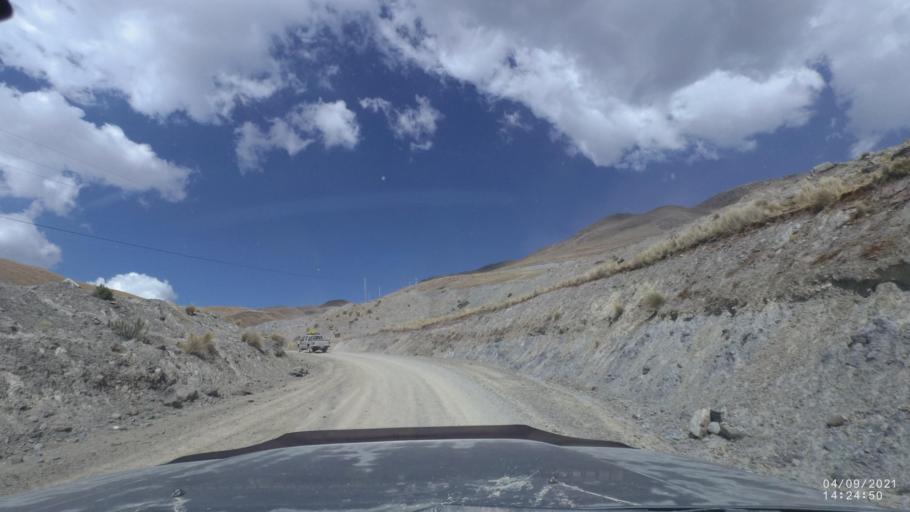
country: BO
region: Cochabamba
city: Sipe Sipe
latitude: -17.2422
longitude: -66.4077
